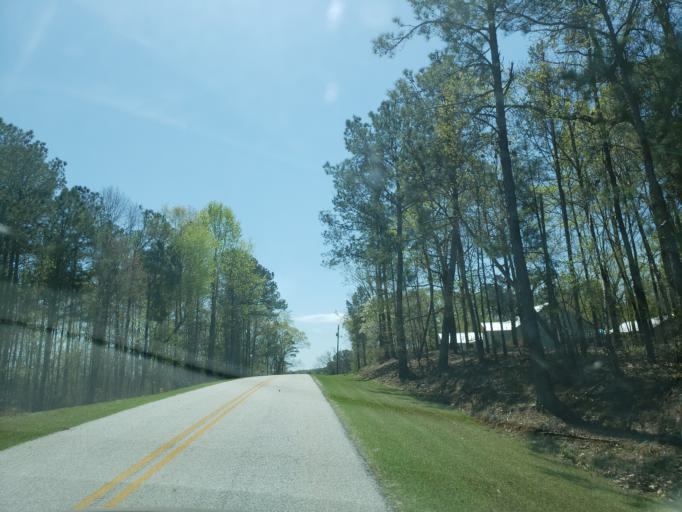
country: US
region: Alabama
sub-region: Elmore County
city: Tallassee
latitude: 32.6786
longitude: -85.8634
